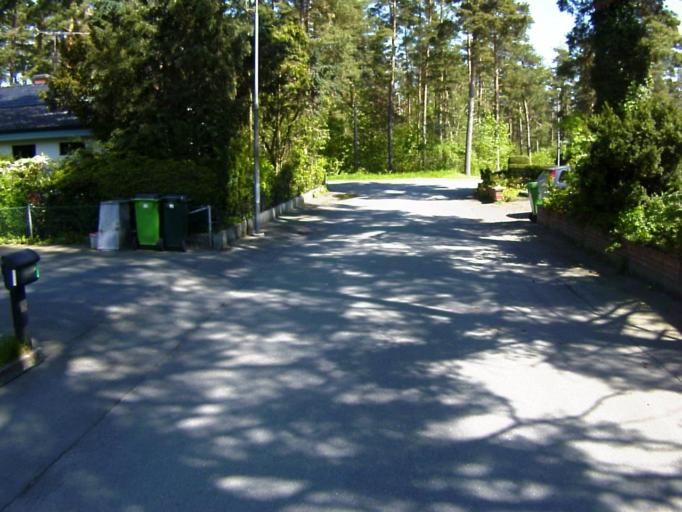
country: SE
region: Skane
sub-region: Kristianstads Kommun
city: Degeberga
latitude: 55.9026
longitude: 14.1006
